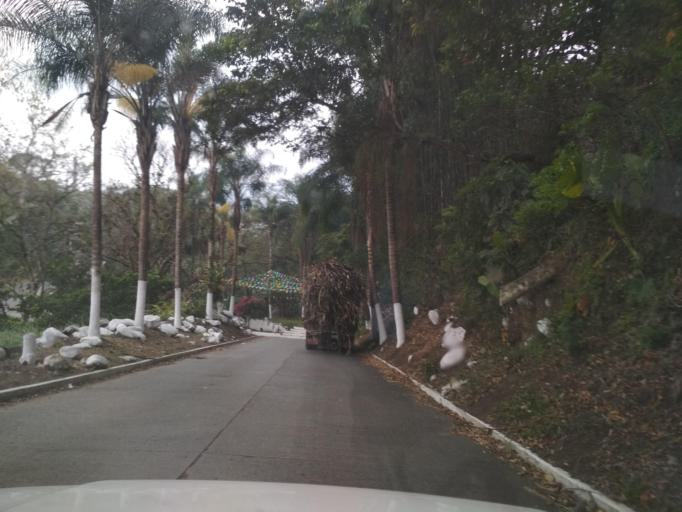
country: MX
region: Veracruz
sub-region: Cordoba
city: San Jose de Tapia
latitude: 18.8385
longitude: -96.9838
